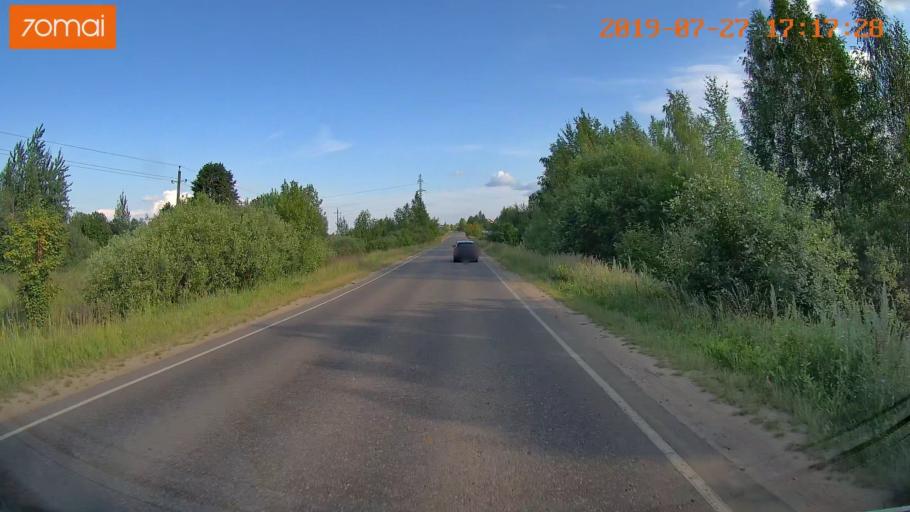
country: RU
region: Ivanovo
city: Novo-Talitsy
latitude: 57.0370
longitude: 40.8948
